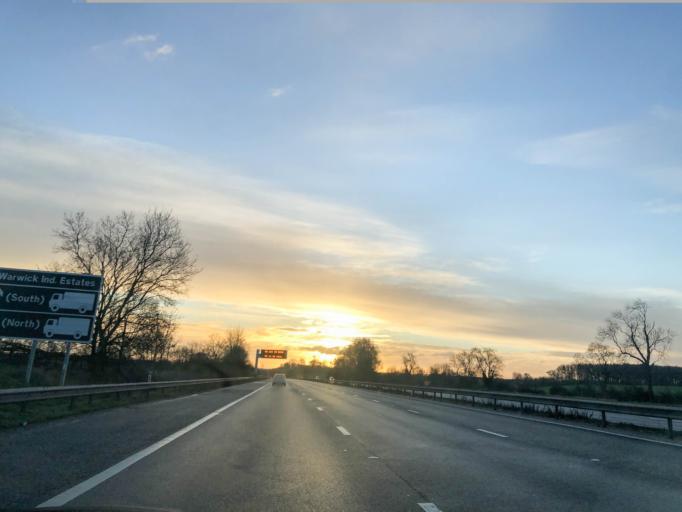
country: GB
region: England
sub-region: Warwickshire
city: Warwick
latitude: 52.2684
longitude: -1.6401
